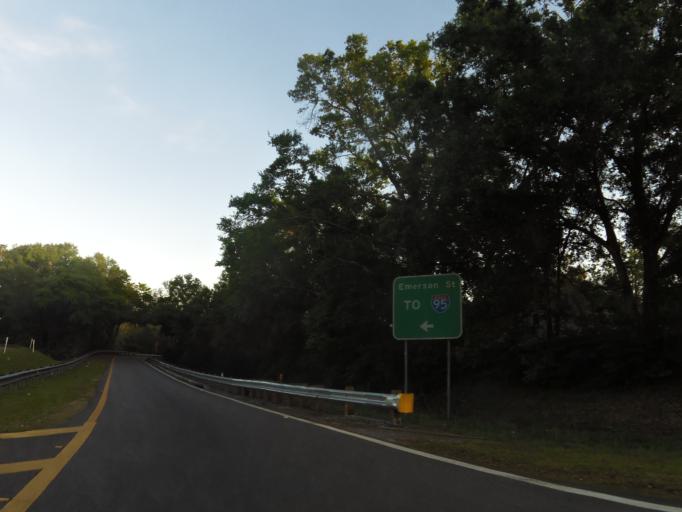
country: US
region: Florida
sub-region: Duval County
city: Jacksonville
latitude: 30.2956
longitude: -81.6163
